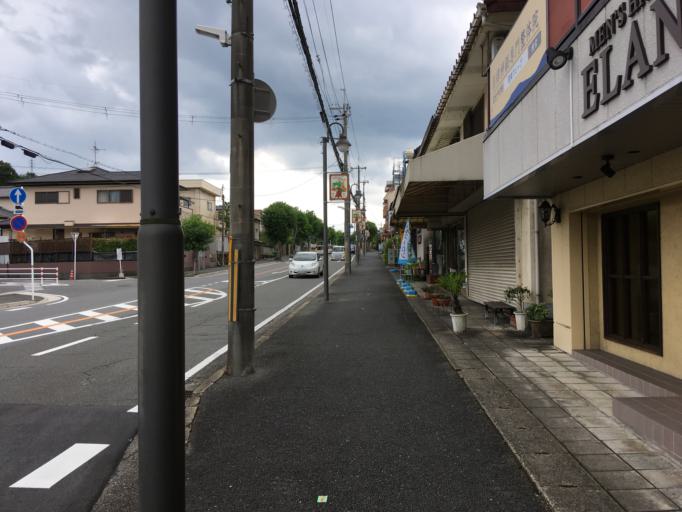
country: JP
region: Nara
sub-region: Ikoma-shi
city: Ikoma
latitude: 34.6851
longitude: 135.7158
